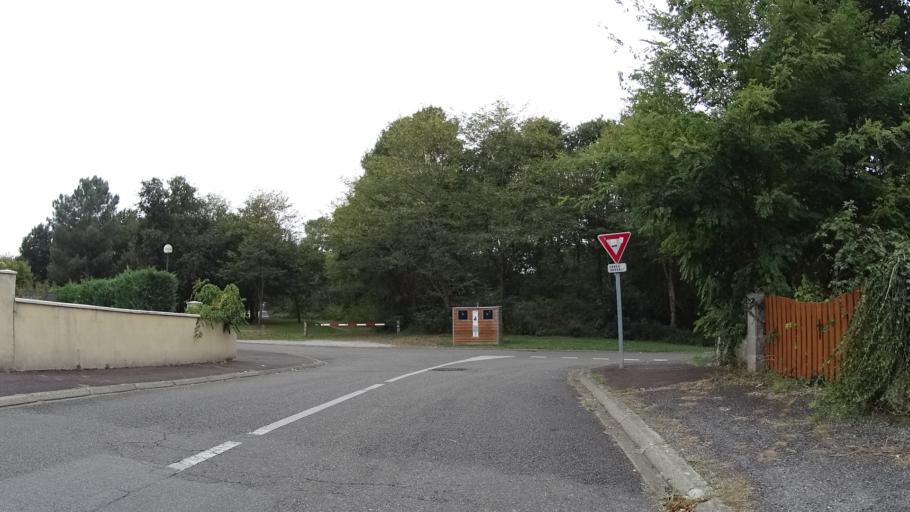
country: FR
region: Aquitaine
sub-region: Departement des Landes
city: Saint-Paul-les-Dax
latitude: 43.7311
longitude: -1.0797
